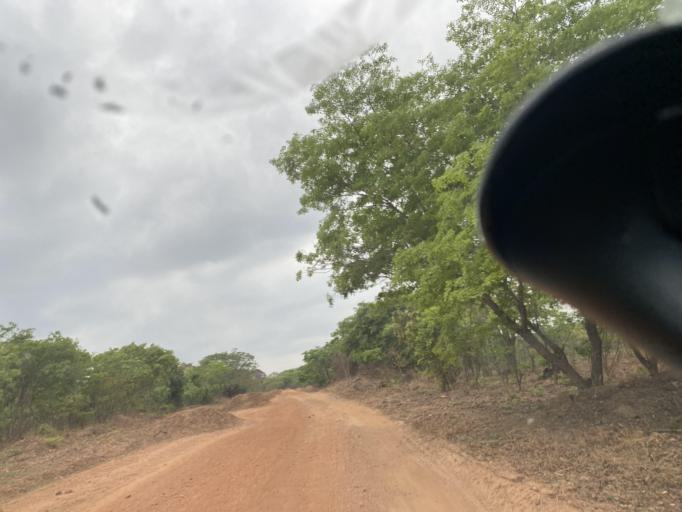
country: ZM
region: Lusaka
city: Chongwe
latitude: -15.2266
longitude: 28.7341
